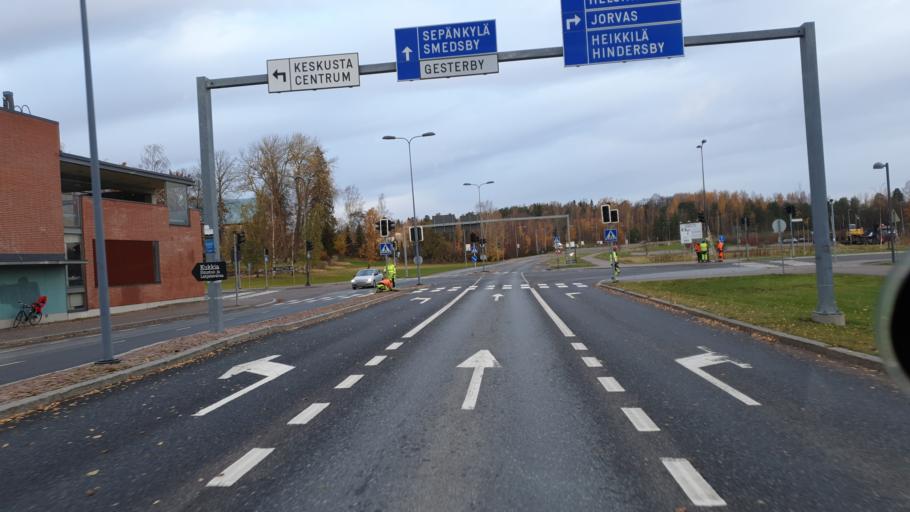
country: FI
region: Uusimaa
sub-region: Helsinki
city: Kirkkonummi
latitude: 60.1232
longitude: 24.4418
